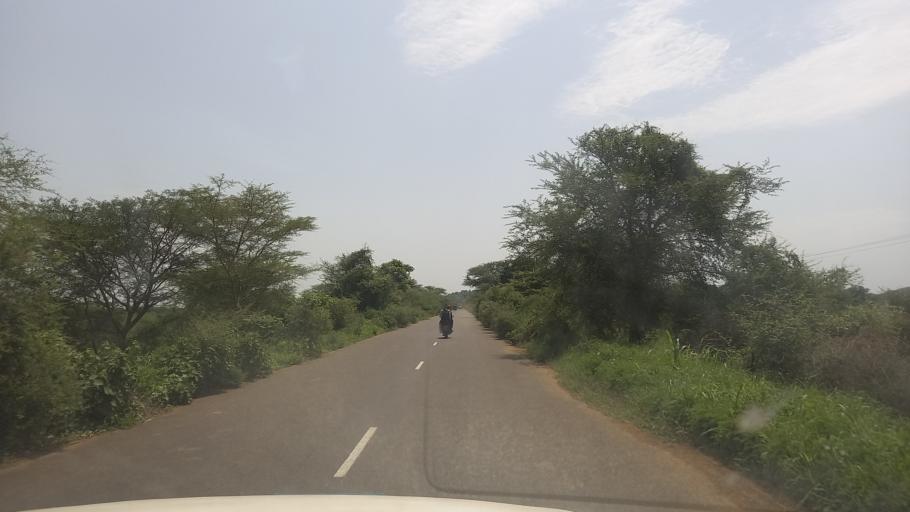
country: ET
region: Gambela
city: Gambela
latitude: 8.2788
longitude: 34.2287
